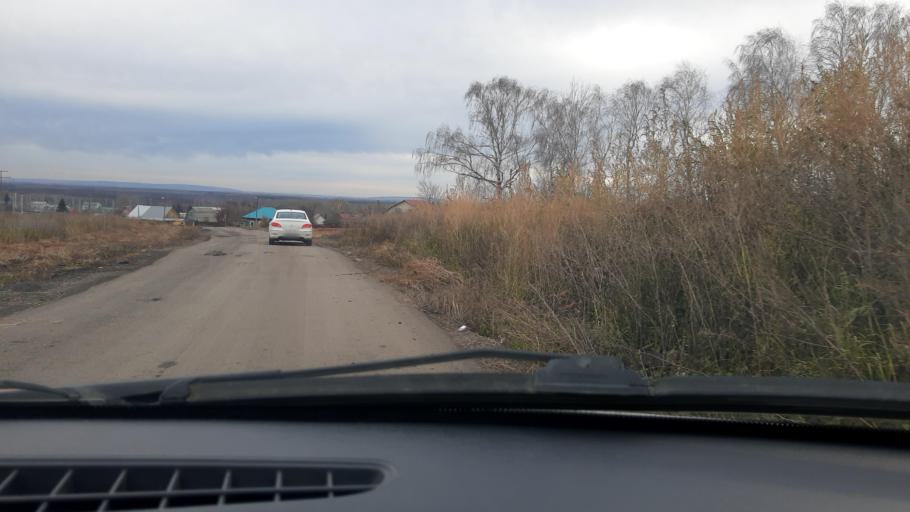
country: RU
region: Bashkortostan
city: Avdon
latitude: 54.6957
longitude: 55.8059
